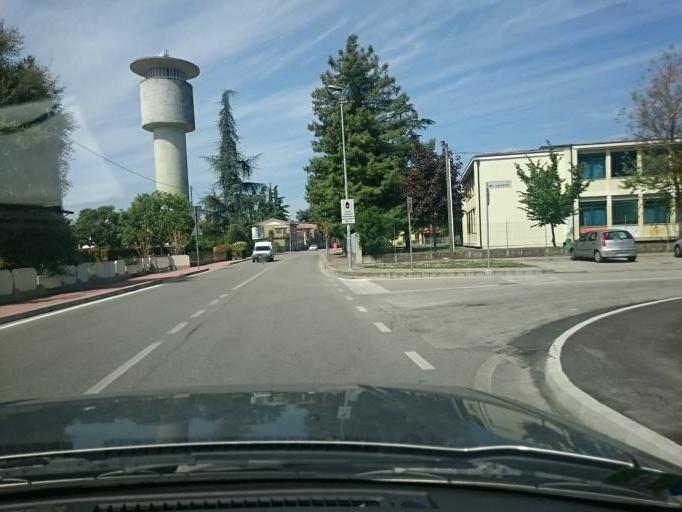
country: IT
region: Veneto
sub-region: Provincia di Padova
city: San Pietro Viminario
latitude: 45.2454
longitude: 11.8226
